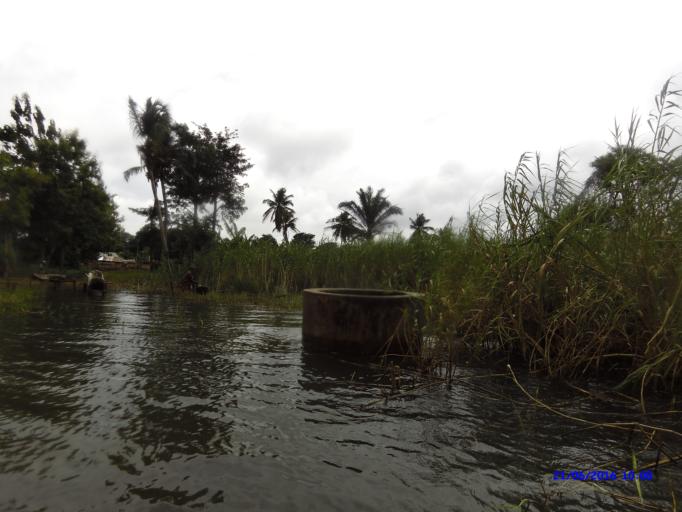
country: BJ
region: Mono
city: Come
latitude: 6.4595
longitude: 1.9267
